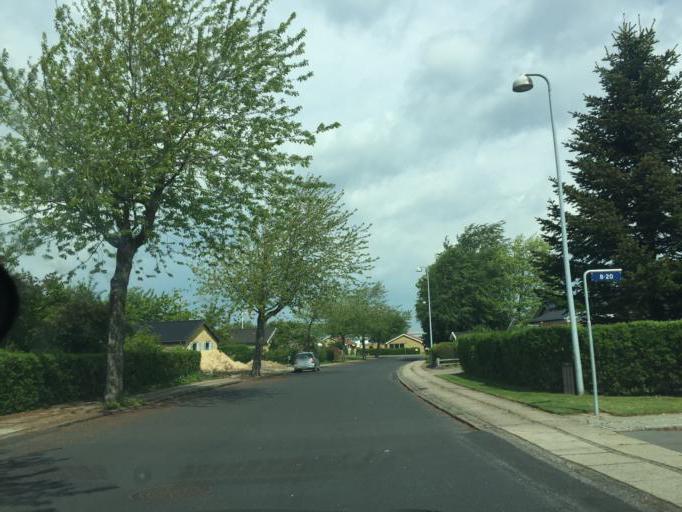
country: DK
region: South Denmark
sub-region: Odense Kommune
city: Odense
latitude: 55.3727
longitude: 10.3528
